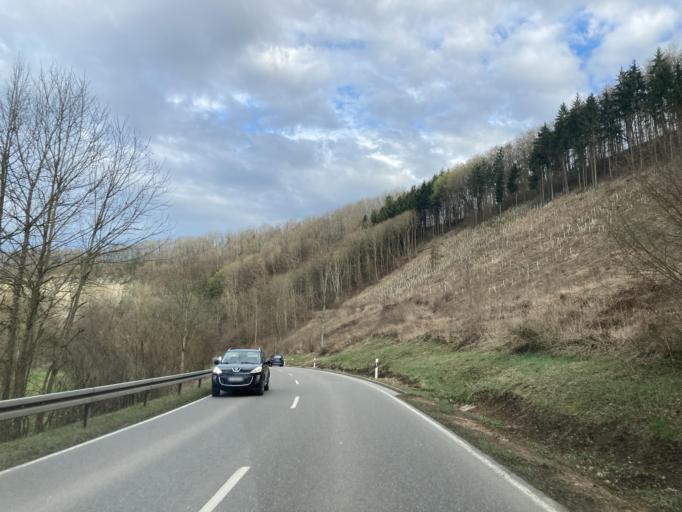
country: DE
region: Baden-Wuerttemberg
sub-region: Tuebingen Region
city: Rottenburg
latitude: 48.4656
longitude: 8.9139
